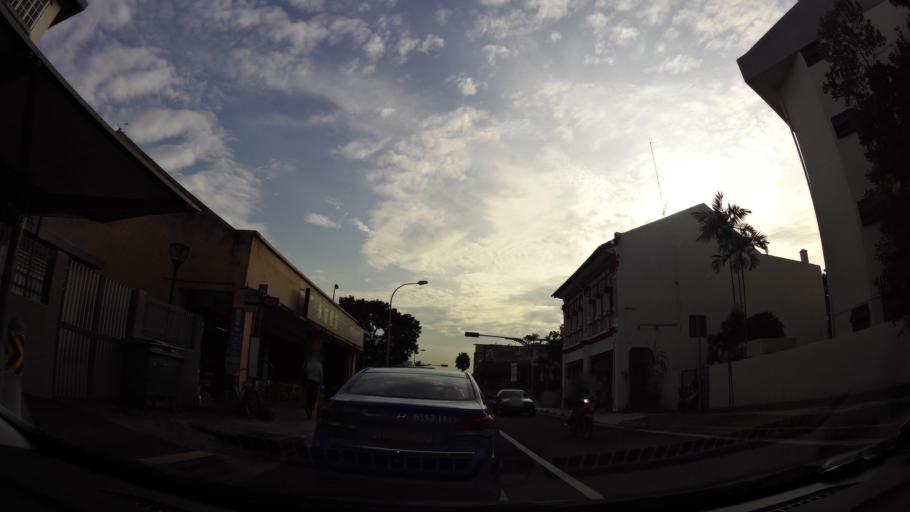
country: SG
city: Singapore
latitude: 1.3143
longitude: 103.9058
